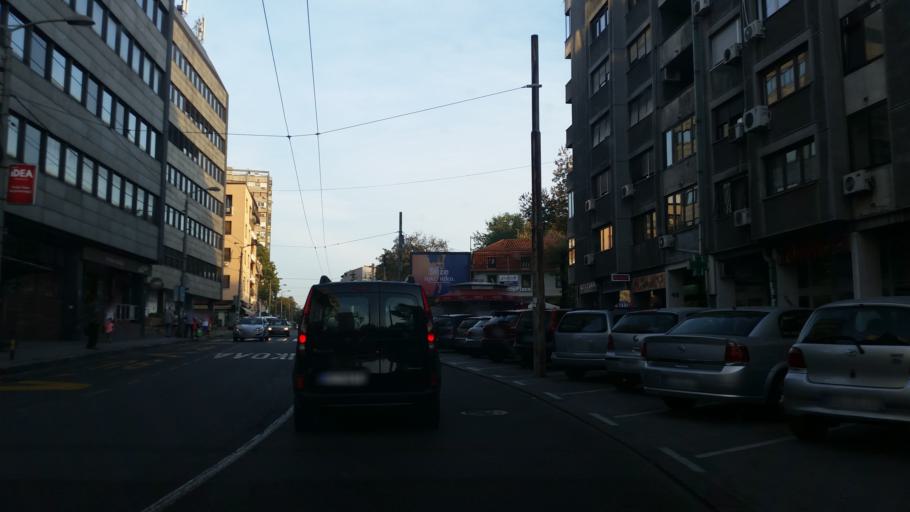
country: RS
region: Central Serbia
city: Belgrade
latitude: 44.8002
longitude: 20.4709
